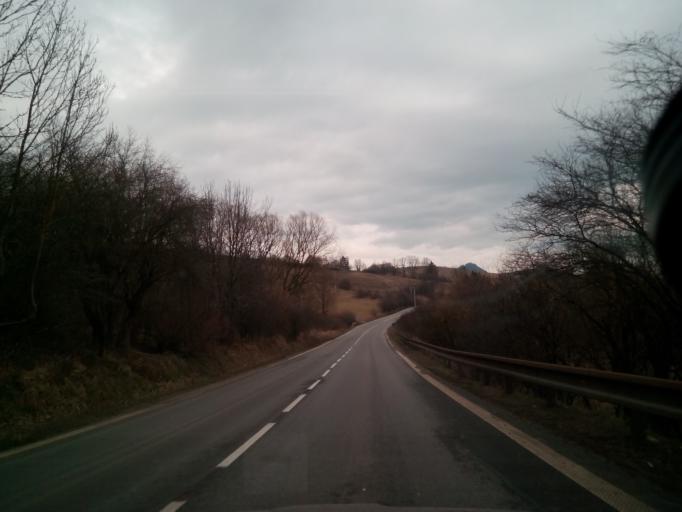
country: SK
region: Zilinsky
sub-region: Okres Dolny Kubin
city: Dolny Kubin
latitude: 49.2055
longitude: 19.2331
